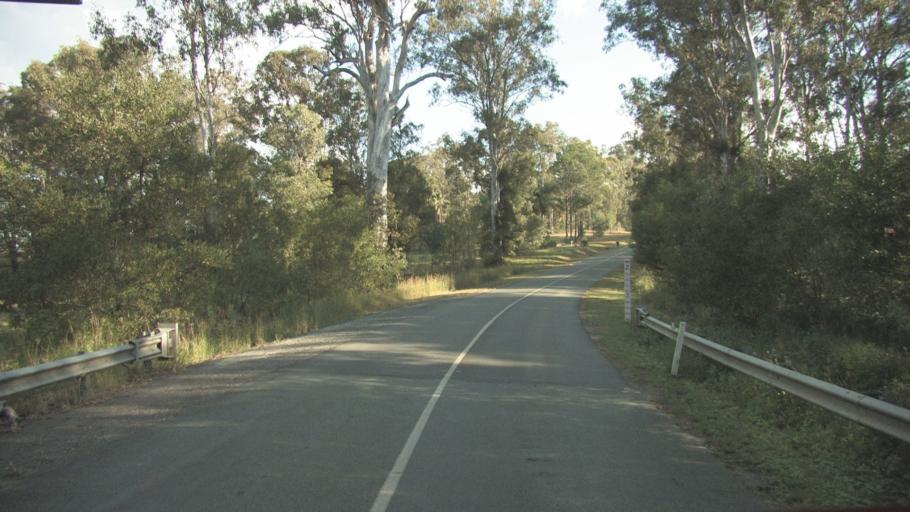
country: AU
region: Queensland
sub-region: Gold Coast
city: Ormeau Hills
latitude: -27.8436
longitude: 153.1559
